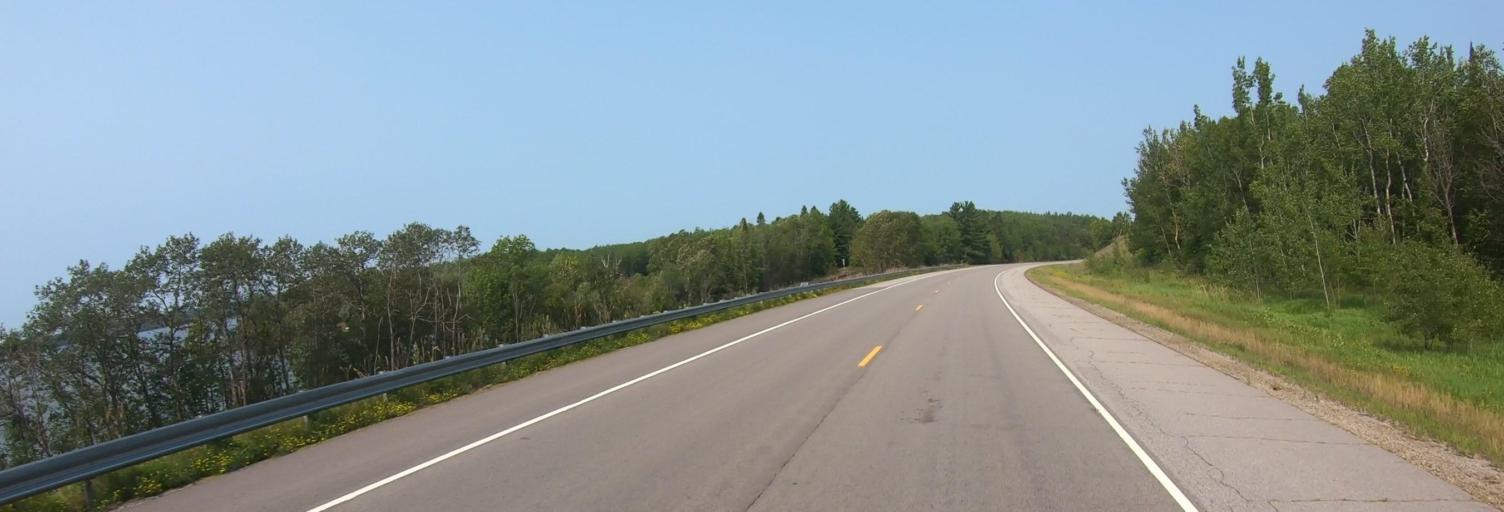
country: CA
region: Ontario
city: Fort Frances
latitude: 48.2201
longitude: -92.9183
